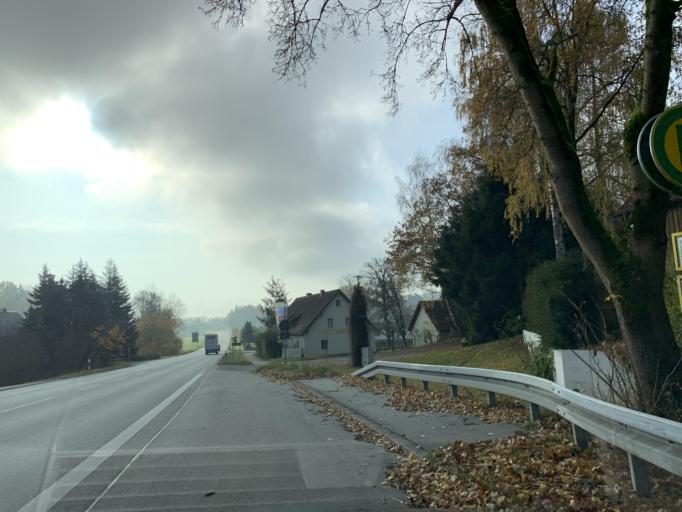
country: DE
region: Bavaria
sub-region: Upper Palatinate
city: Bruck in der Oberpfalz
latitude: 49.2638
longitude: 12.2954
